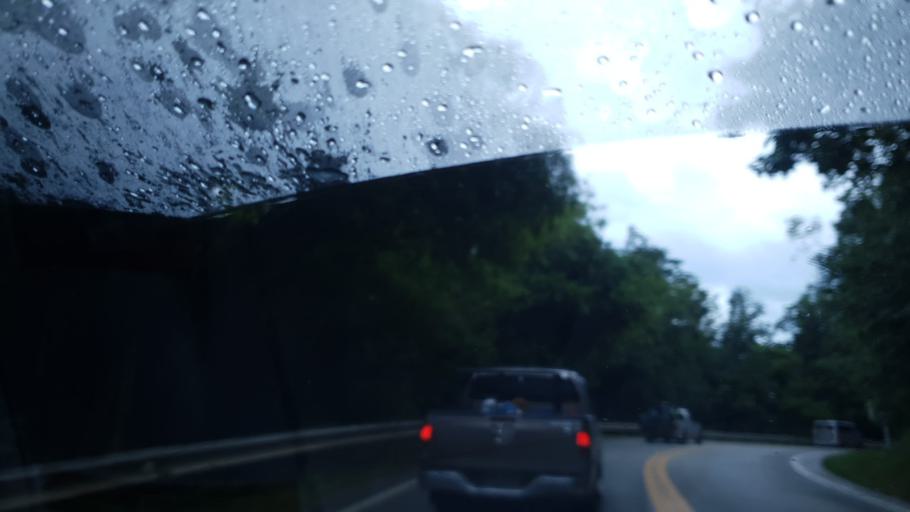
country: TH
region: Chiang Mai
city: Hot
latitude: 18.2235
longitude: 98.4829
